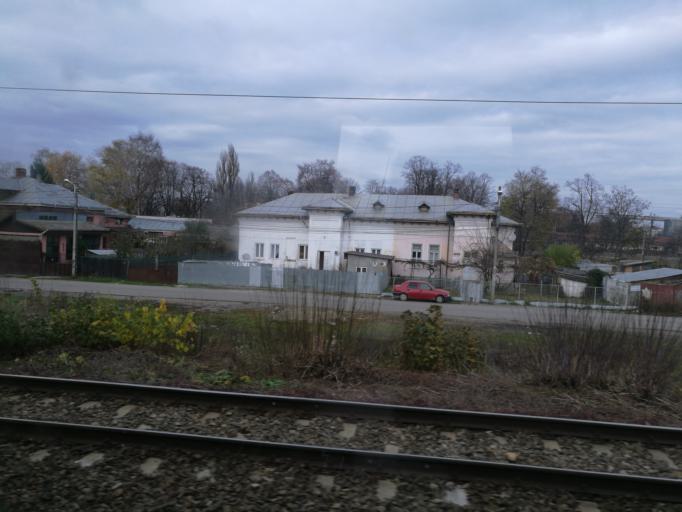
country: RO
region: Neamt
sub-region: Municipiul Roman
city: Roman
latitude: 46.9300
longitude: 26.9174
